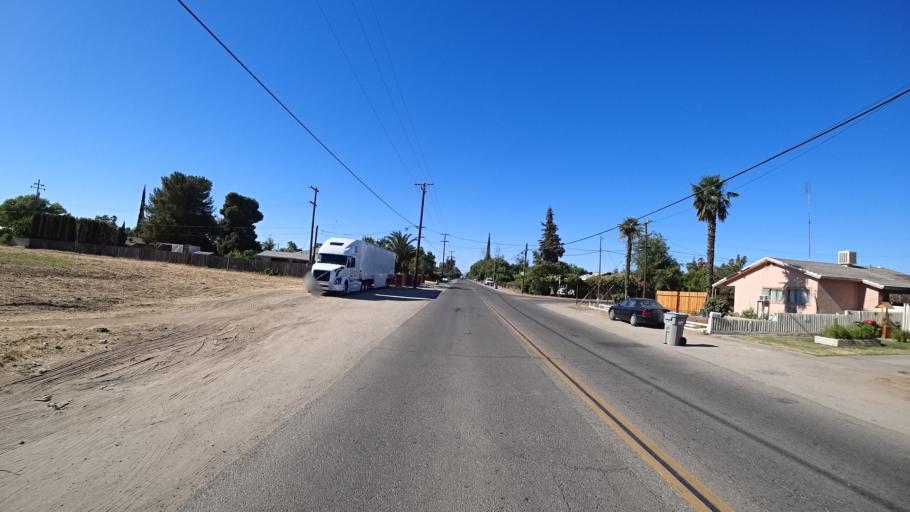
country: US
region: California
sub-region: Fresno County
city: West Park
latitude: 36.7560
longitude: -119.8356
